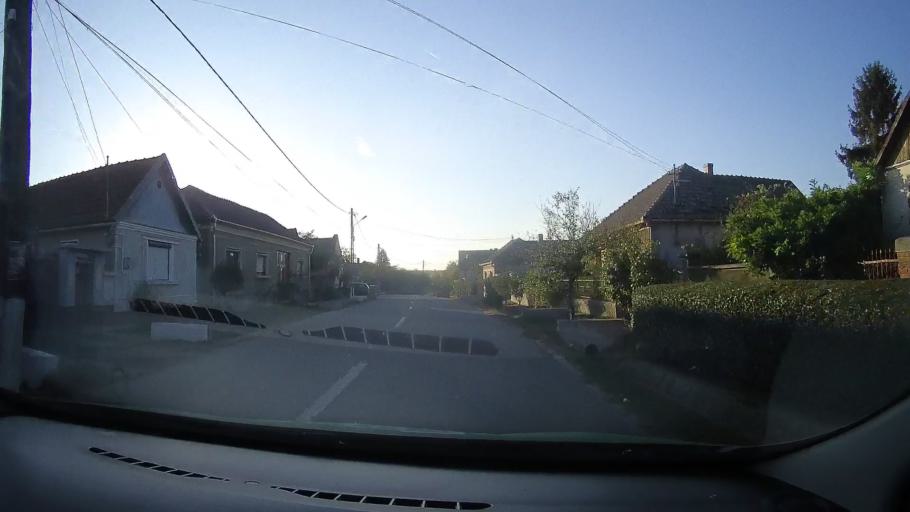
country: RO
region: Bihor
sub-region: Comuna Cetariu
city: Cetariu
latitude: 47.1477
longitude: 21.9971
